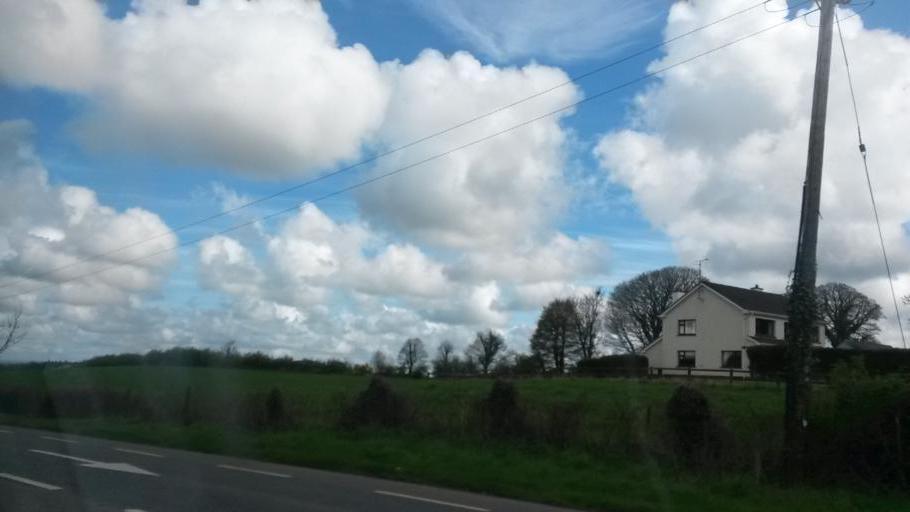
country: IE
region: Ulster
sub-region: An Cabhan
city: Ballyjamesduff
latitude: 53.9348
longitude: -7.2189
